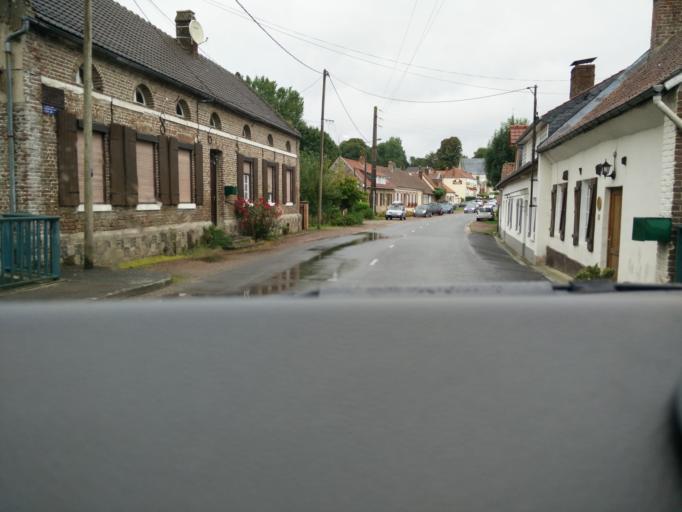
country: FR
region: Nord-Pas-de-Calais
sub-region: Departement du Pas-de-Calais
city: Campagne-les-Hesdin
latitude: 50.3314
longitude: 1.8737
